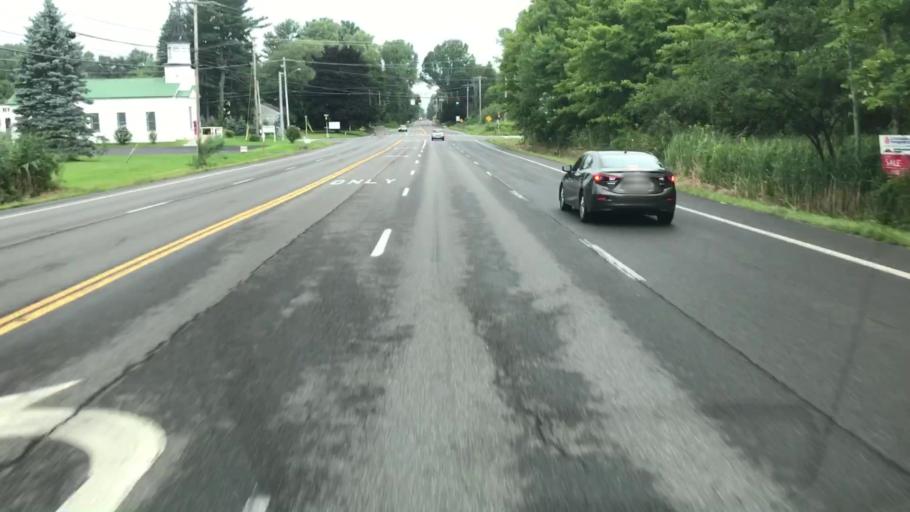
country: US
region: New York
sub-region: Onondaga County
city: Liverpool
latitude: 43.1493
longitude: -76.2074
